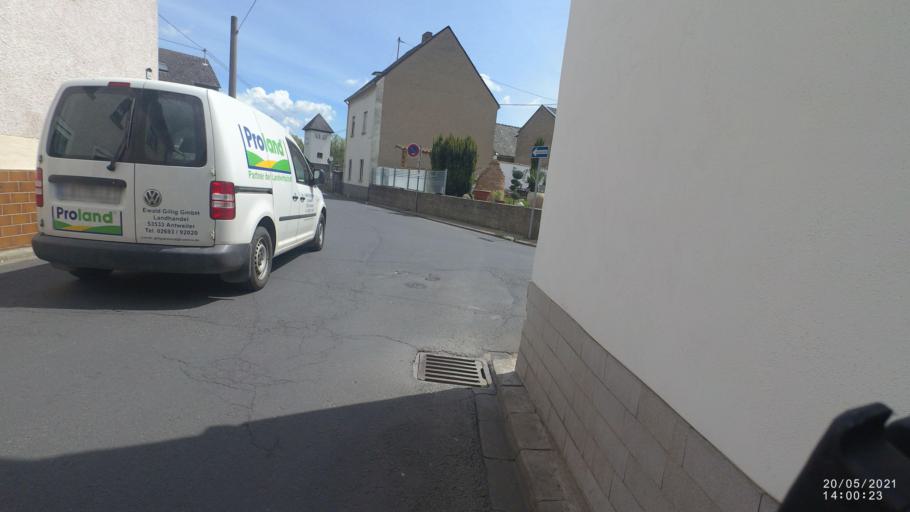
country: DE
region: Rheinland-Pfalz
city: Saffig
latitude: 50.4000
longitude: 7.4133
